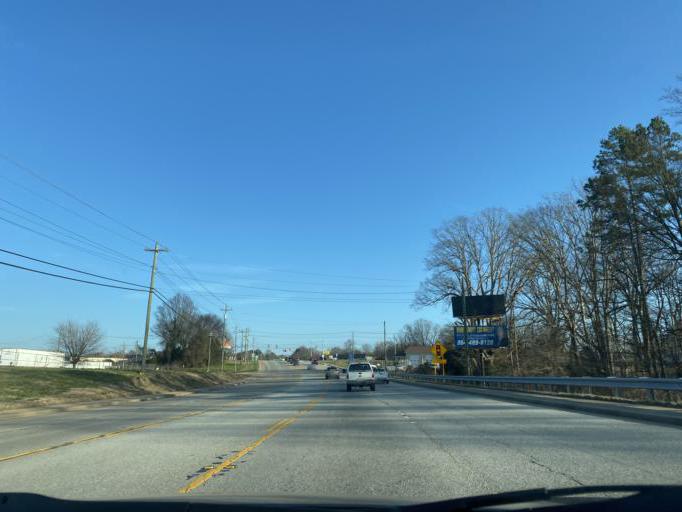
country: US
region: South Carolina
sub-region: Cherokee County
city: Gaffney
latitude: 35.0658
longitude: -81.6664
